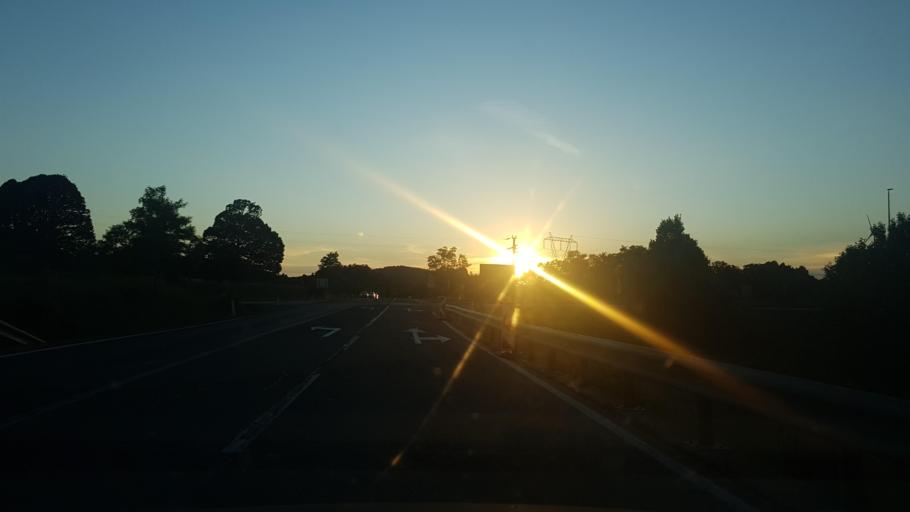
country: SI
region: Divaca
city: Divaca
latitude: 45.7208
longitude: 14.0059
